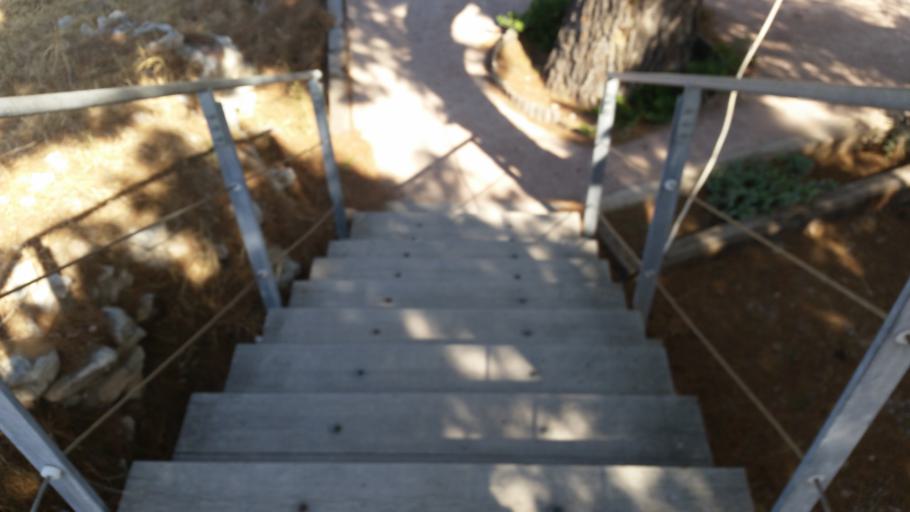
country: GR
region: Peloponnese
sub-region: Nomos Argolidos
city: Tolon
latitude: 37.5282
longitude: 22.8730
